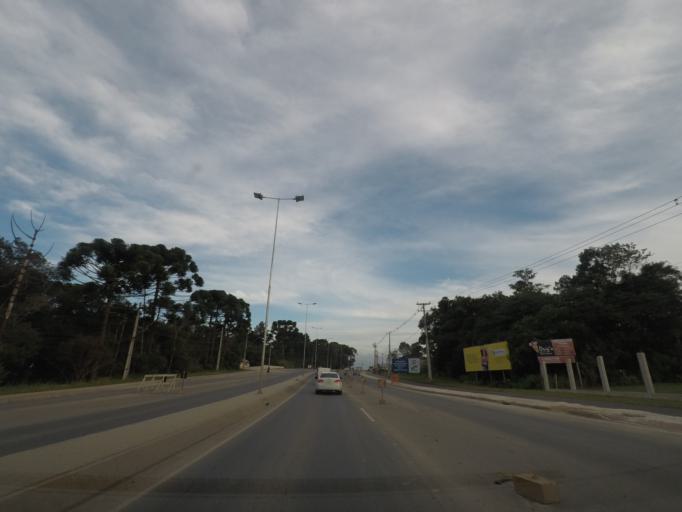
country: BR
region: Parana
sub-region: Colombo
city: Colombo
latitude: -25.3171
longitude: -49.2205
